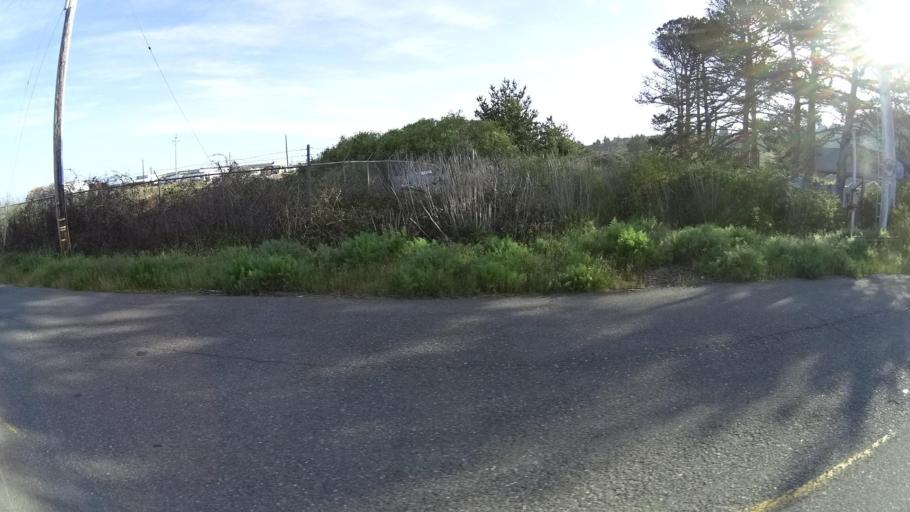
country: US
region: California
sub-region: Humboldt County
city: Humboldt Hill
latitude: 40.7256
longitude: -124.2189
